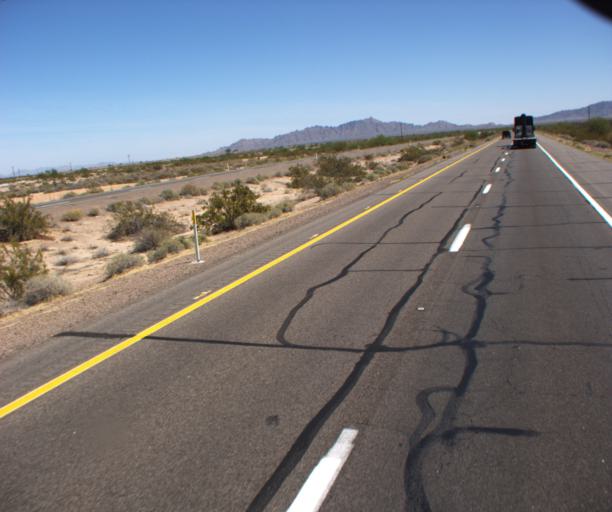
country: US
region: Arizona
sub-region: Yuma County
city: Wellton
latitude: 32.7020
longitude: -113.8967
